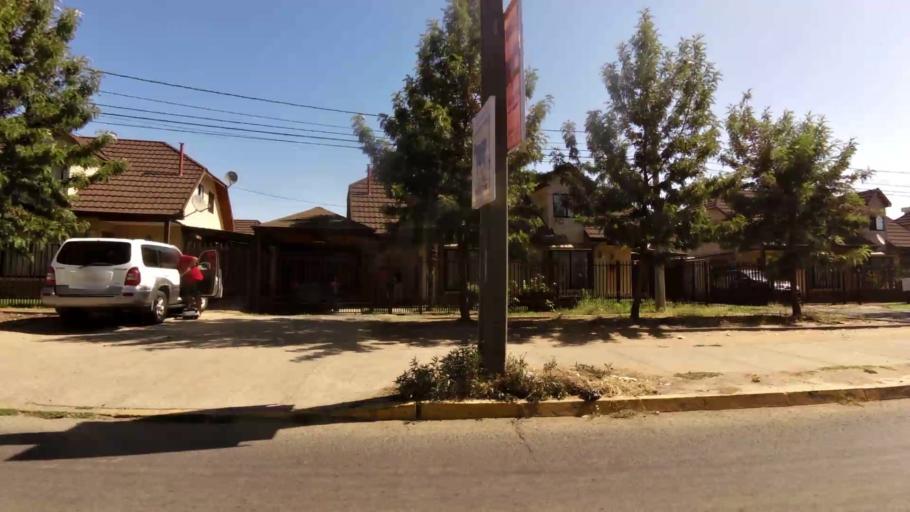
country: CL
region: Maule
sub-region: Provincia de Talca
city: Talca
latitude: -35.4278
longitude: -71.6250
